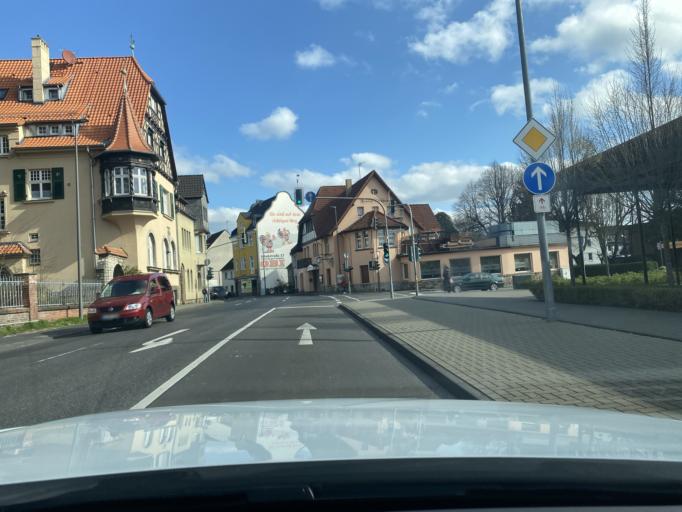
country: DE
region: North Rhine-Westphalia
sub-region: Regierungsbezirk Koln
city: Bergisch Gladbach
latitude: 50.9847
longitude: 7.1202
